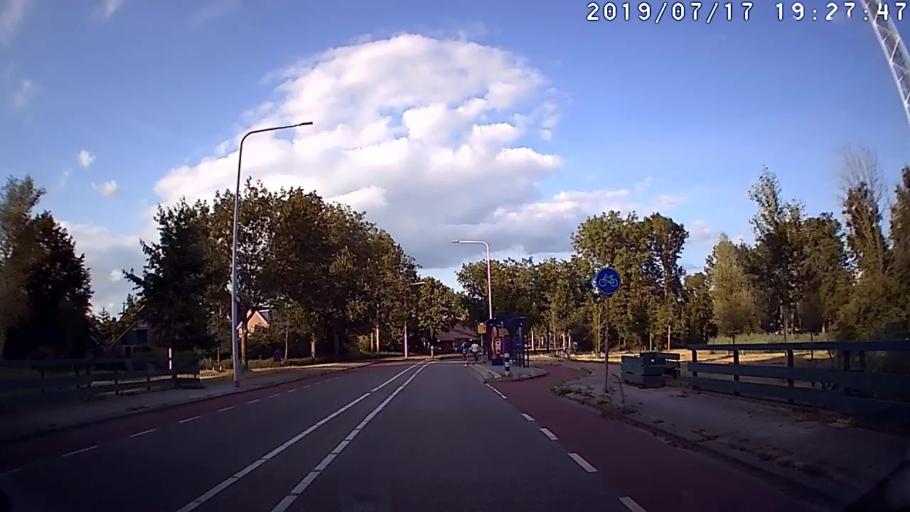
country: NL
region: Overijssel
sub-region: Gemeente Zwolle
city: Zwolle
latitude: 52.5352
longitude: 6.1059
